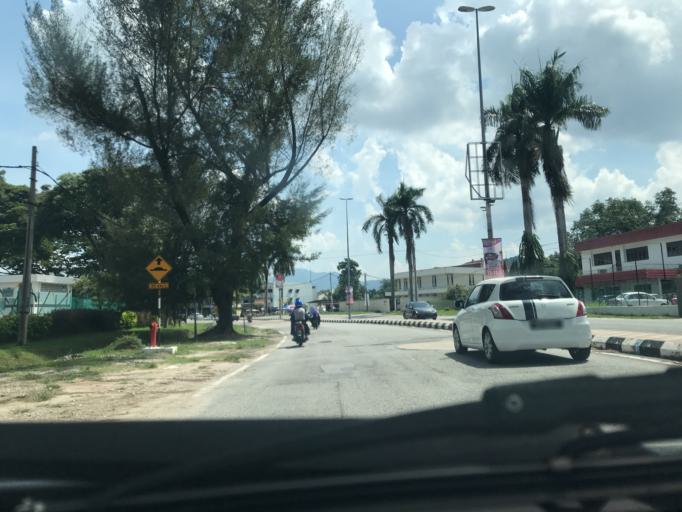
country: MY
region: Perak
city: Ipoh
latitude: 4.6113
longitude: 101.1020
